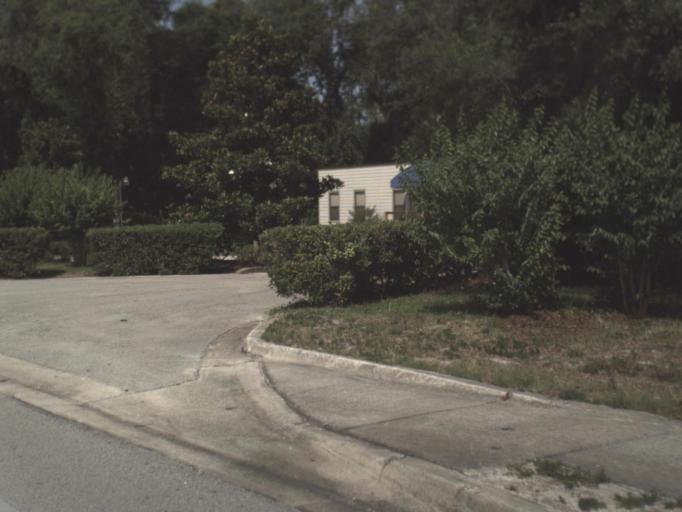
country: US
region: Florida
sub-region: Saint Johns County
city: Saint Augustine South
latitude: 29.8501
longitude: -81.3588
